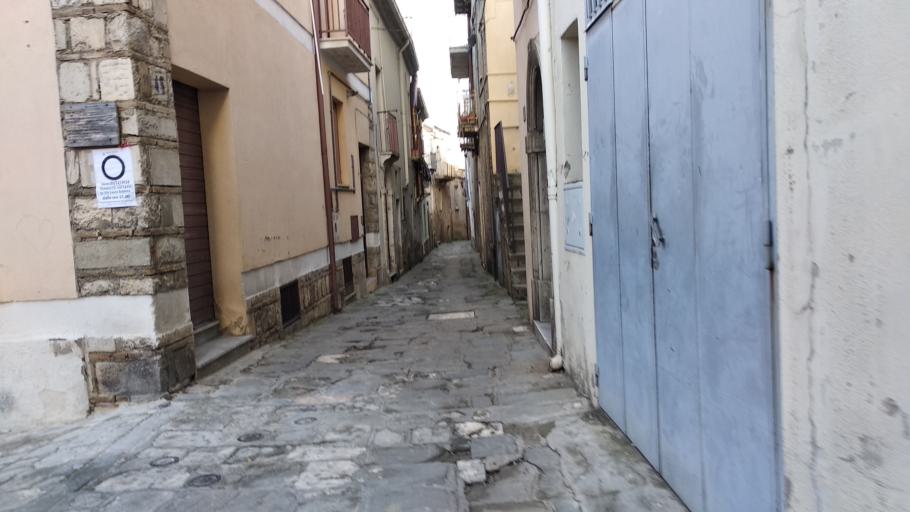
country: IT
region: Basilicate
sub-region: Provincia di Matera
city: Tricarico
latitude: 40.6244
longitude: 16.1436
